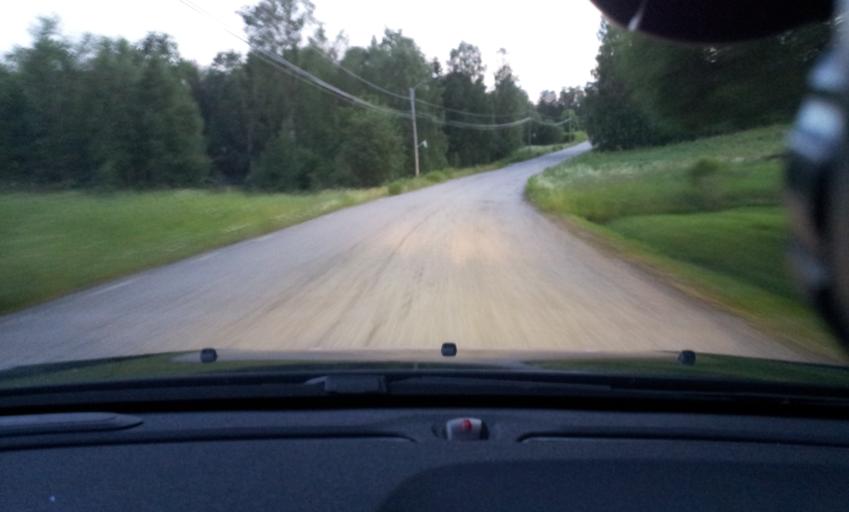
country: SE
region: Vaesternorrland
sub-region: Ange Kommun
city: Fransta
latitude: 62.7794
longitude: 16.0241
